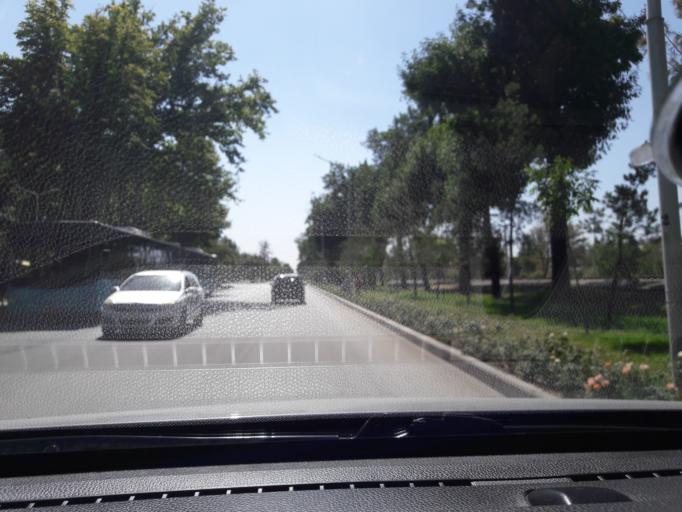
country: TJ
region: Dushanbe
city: Dushanbe
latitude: 38.5685
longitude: 68.7493
